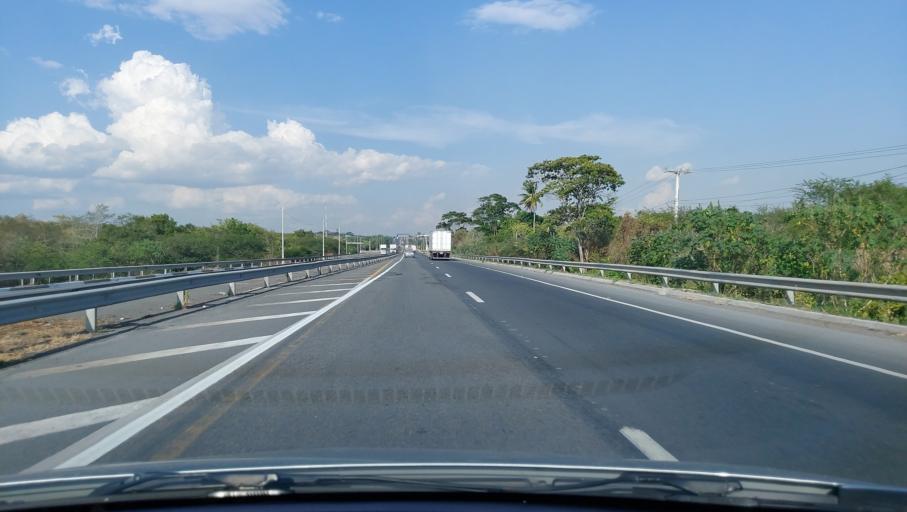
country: BR
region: Bahia
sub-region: Santo Estevao
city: Santo Estevao
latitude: -12.4082
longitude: -39.1791
